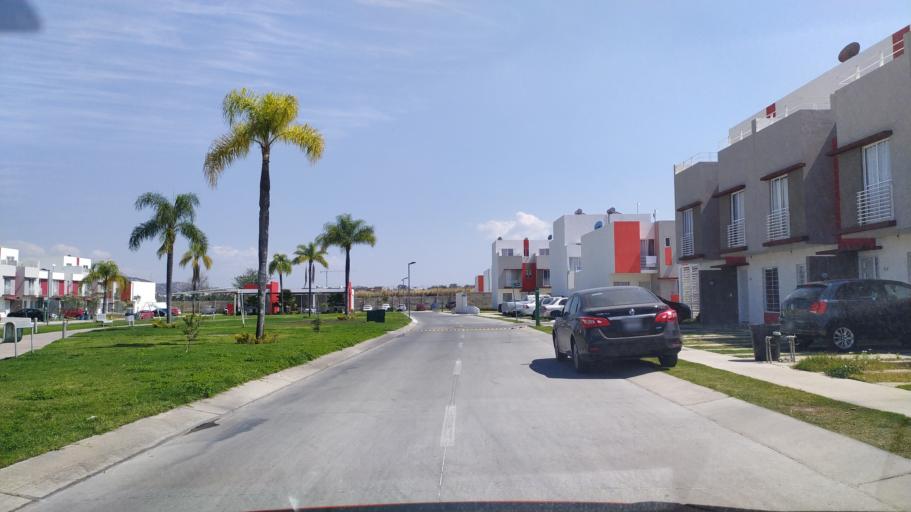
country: MX
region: Jalisco
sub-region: Zapopan
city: Campo Real
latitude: 20.7761
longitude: -103.4314
